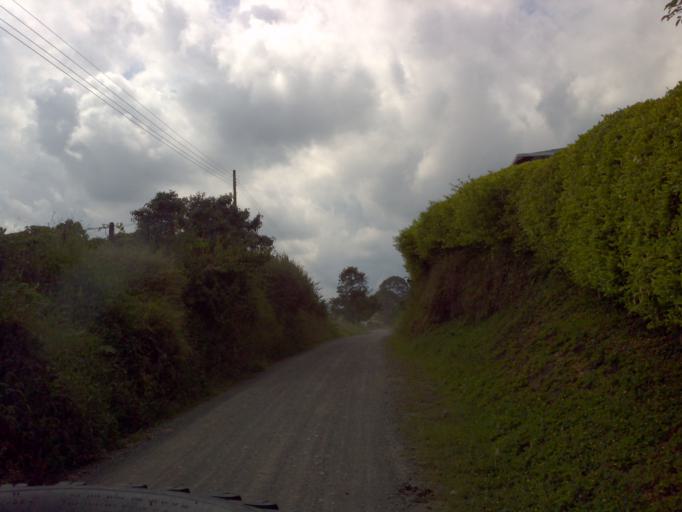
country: CO
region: Valle del Cauca
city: Ulloa
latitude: 4.7342
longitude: -75.7024
